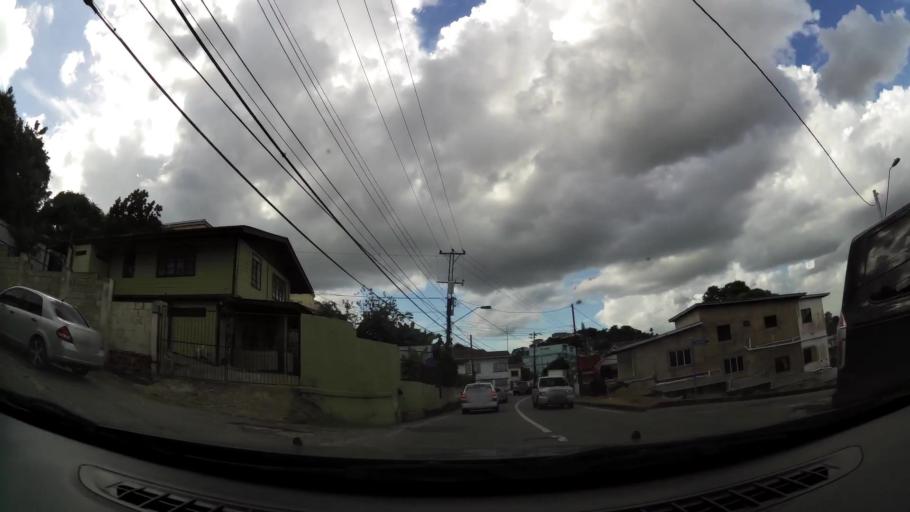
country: TT
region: City of San Fernando
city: Mon Repos
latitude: 10.2852
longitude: -61.4548
